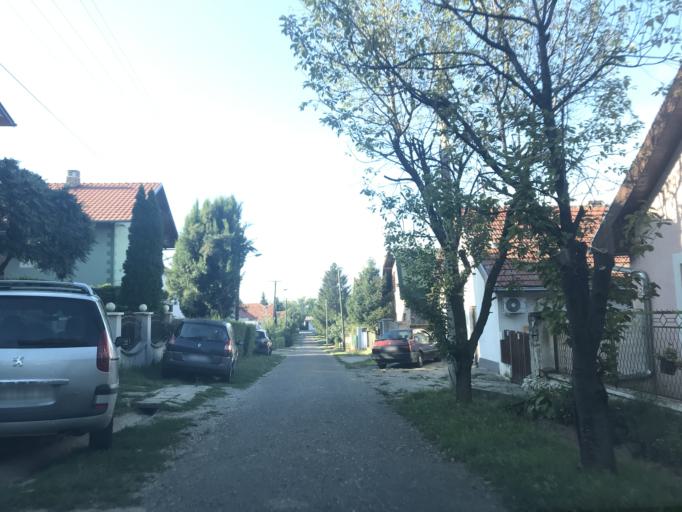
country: RS
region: Autonomna Pokrajina Vojvodina
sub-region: Juznobacki Okrug
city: Novi Sad
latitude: 45.2121
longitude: 19.8036
